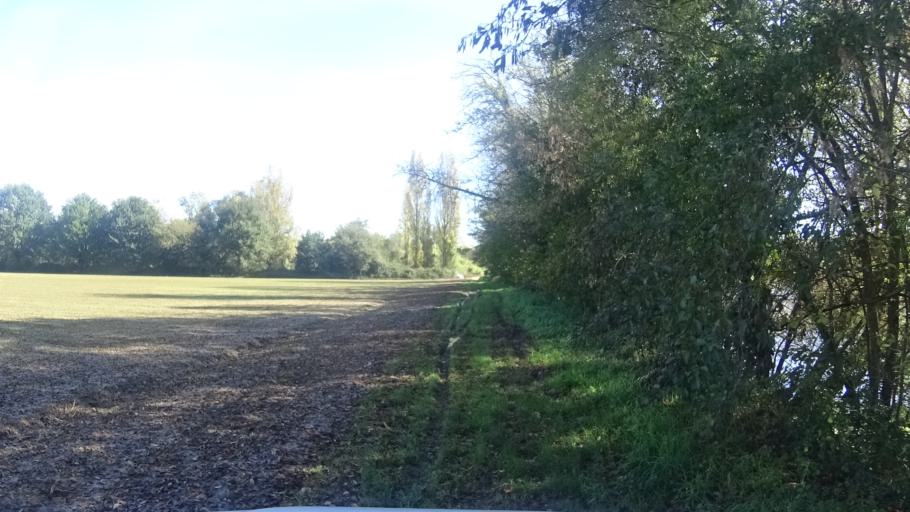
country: FR
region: Aquitaine
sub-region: Departement de la Dordogne
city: Saint-Cyprien
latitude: 44.8565
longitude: 1.0344
